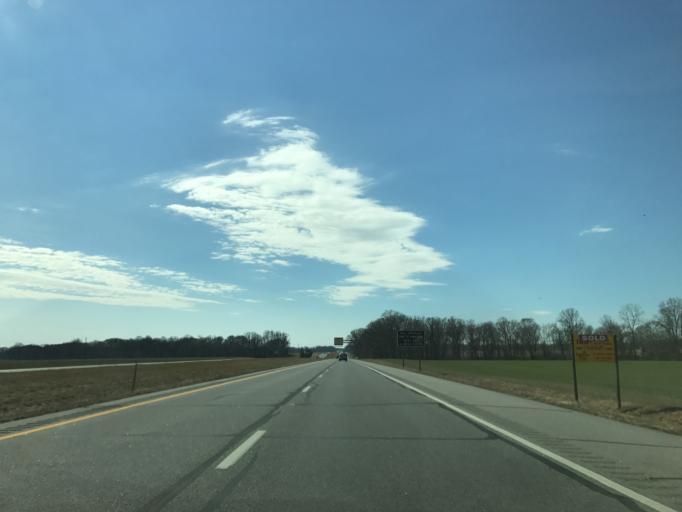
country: US
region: Delaware
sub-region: New Castle County
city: Middletown
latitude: 39.3951
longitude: -75.7884
